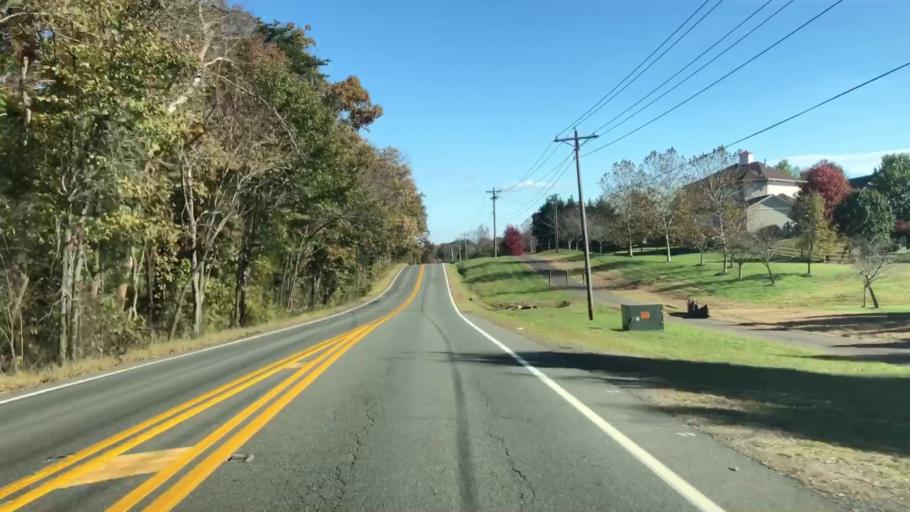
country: US
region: Virginia
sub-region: Fauquier County
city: New Baltimore
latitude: 38.7536
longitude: -77.6668
